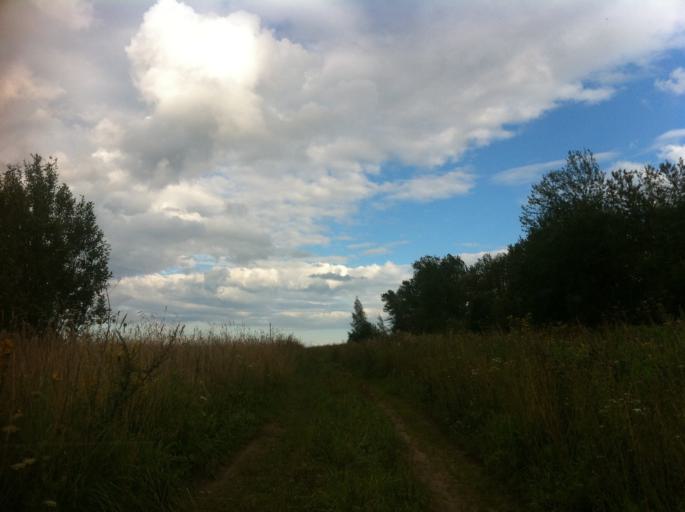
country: RU
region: Pskov
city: Izborsk
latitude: 57.8186
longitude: 27.9743
